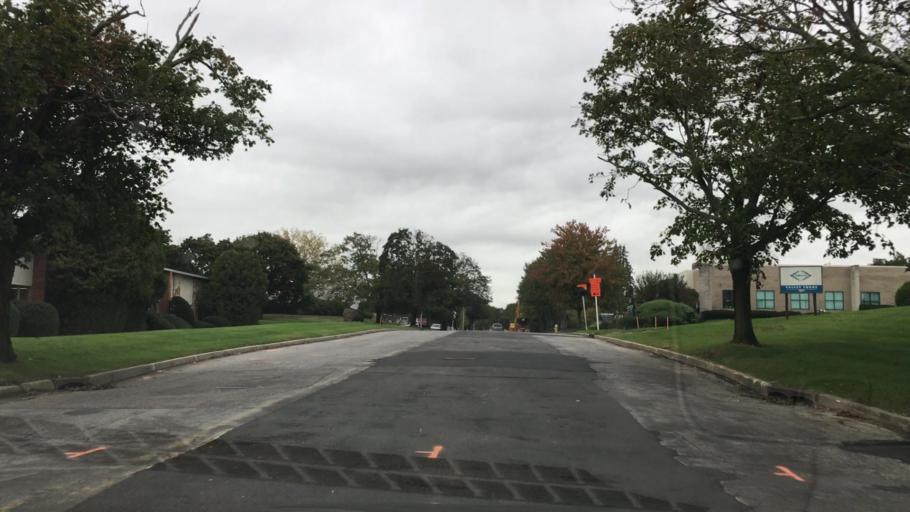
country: US
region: New York
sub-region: Suffolk County
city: Brentwood
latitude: 40.8147
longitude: -73.2432
